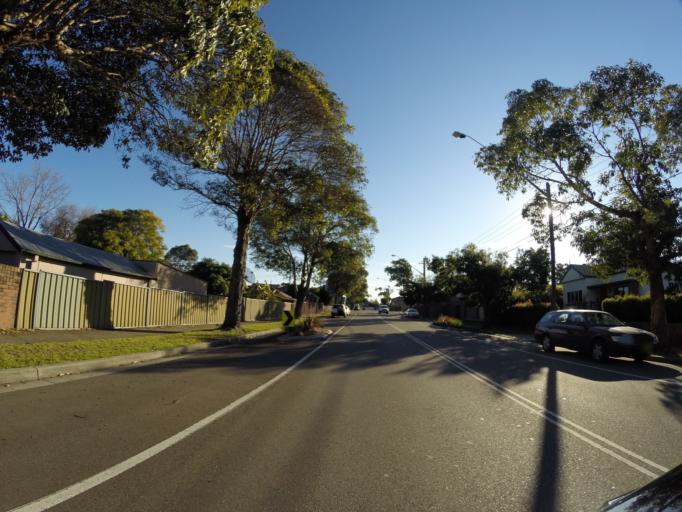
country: AU
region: New South Wales
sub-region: Auburn
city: Lidcombe
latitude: -33.8636
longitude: 151.0320
